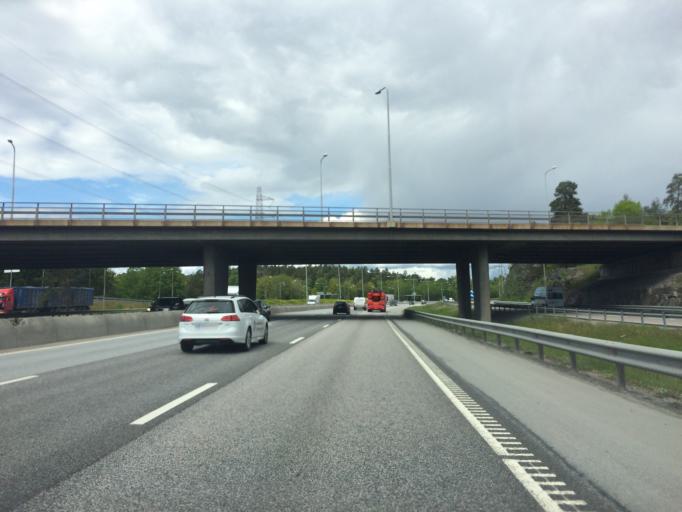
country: SE
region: Stockholm
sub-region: Huddinge Kommun
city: Segeltorp
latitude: 59.2734
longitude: 17.9137
